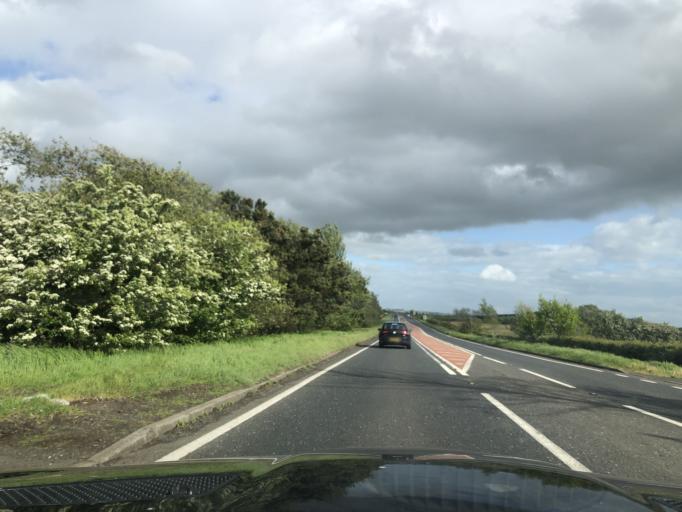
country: GB
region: Northern Ireland
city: Dunloy
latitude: 55.0338
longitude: -6.4039
